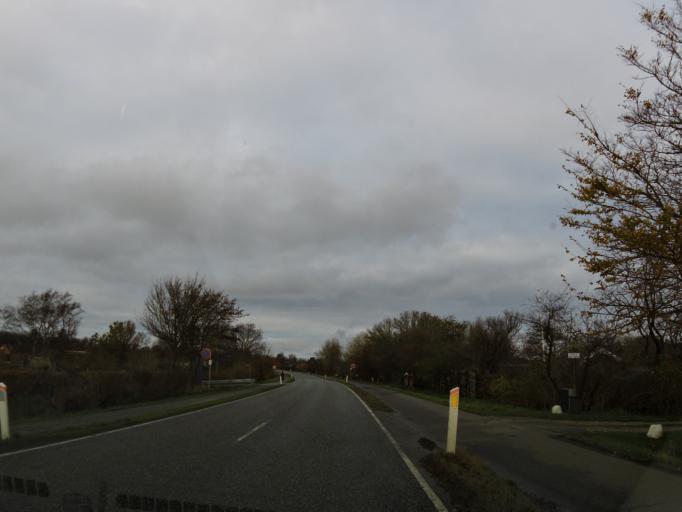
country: DK
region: Central Jutland
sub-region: Arhus Kommune
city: Malling
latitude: 55.9817
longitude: 10.2504
